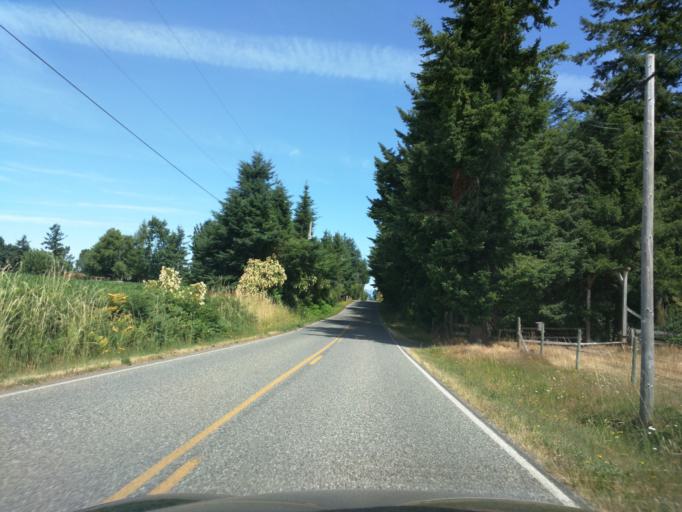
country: US
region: Washington
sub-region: Whatcom County
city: Everson
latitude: 48.8826
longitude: -122.3977
